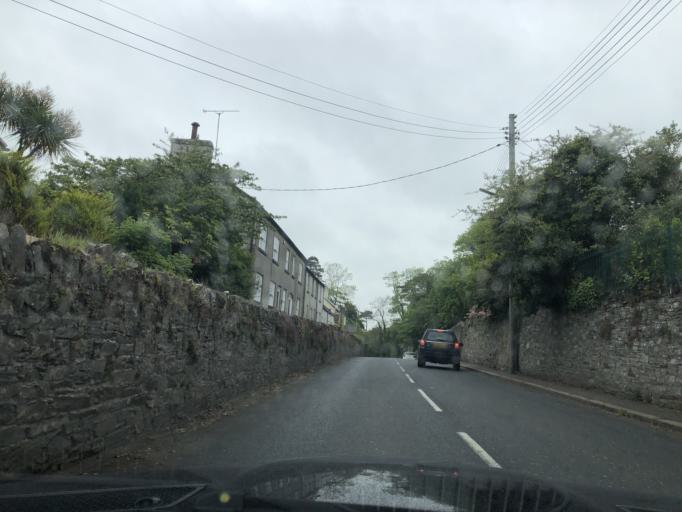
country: GB
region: Northern Ireland
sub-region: Down District
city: Portaferry
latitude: 54.3690
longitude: -5.5582
